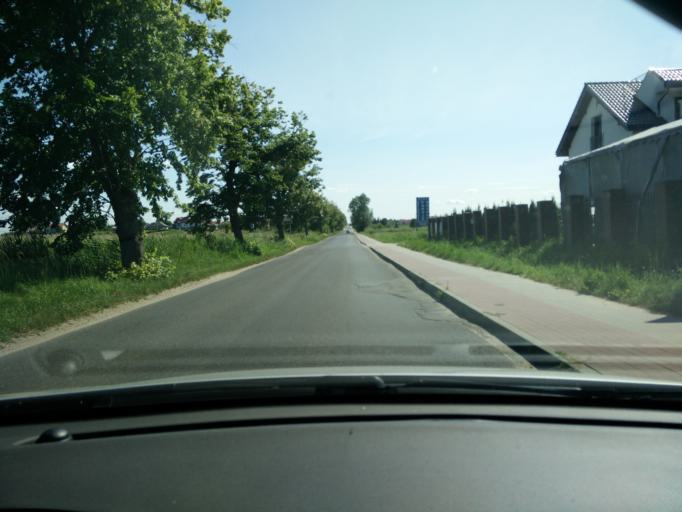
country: PL
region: Pomeranian Voivodeship
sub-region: Powiat pucki
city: Mosty
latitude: 54.6267
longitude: 18.4966
